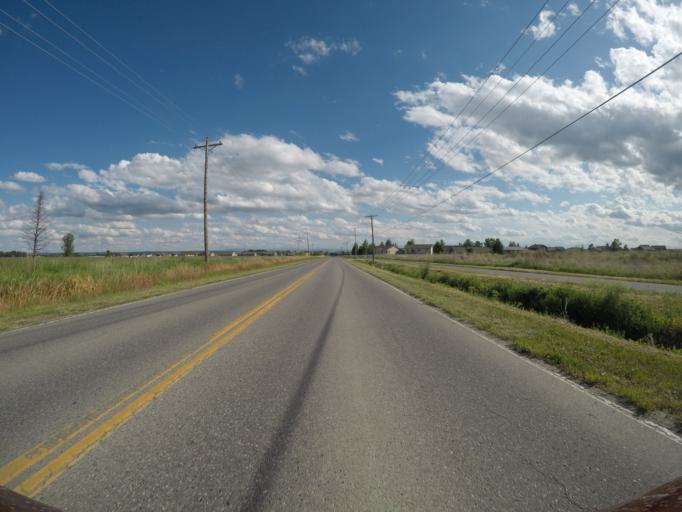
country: US
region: Montana
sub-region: Yellowstone County
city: Billings
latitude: 45.7925
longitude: -108.6527
